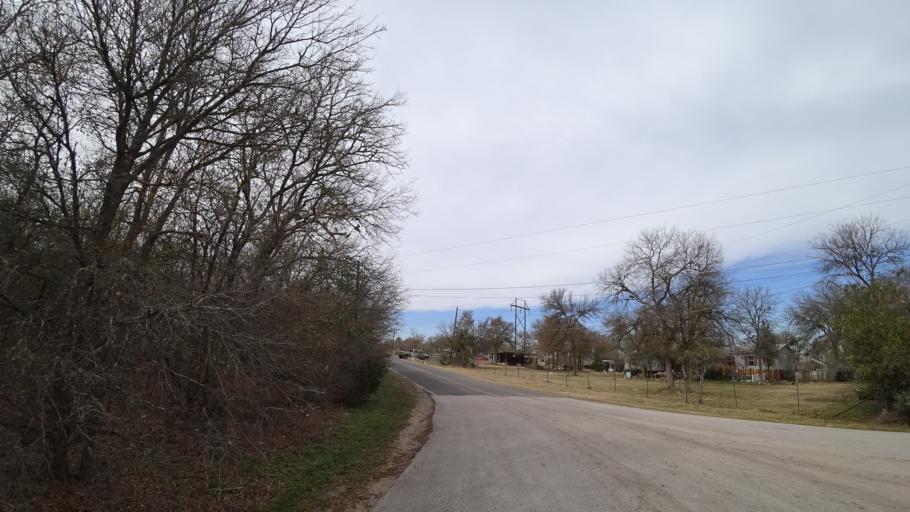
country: US
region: Texas
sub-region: Travis County
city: Garfield
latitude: 30.1401
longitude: -97.5733
